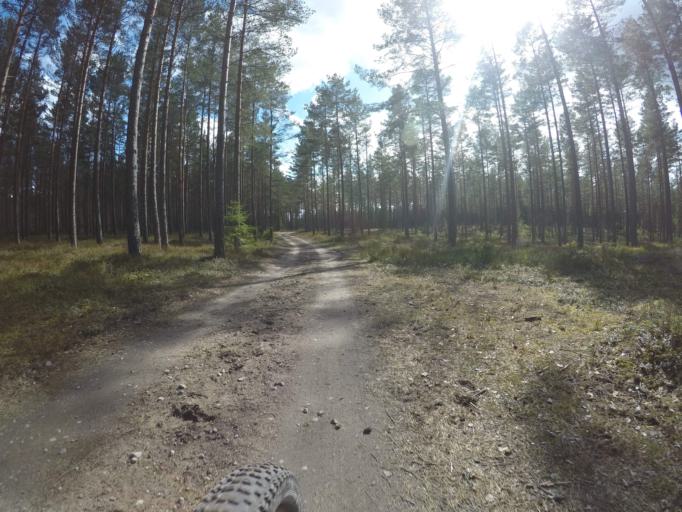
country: SE
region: Vaestmanland
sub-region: Kungsors Kommun
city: Kungsoer
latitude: 59.3614
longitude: 16.1088
